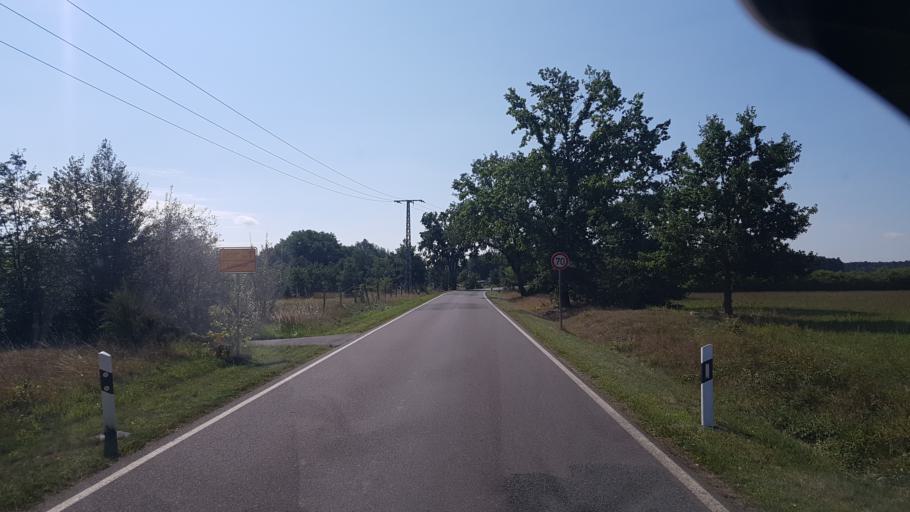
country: DE
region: Brandenburg
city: Vetschau
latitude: 51.7101
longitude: 14.0888
